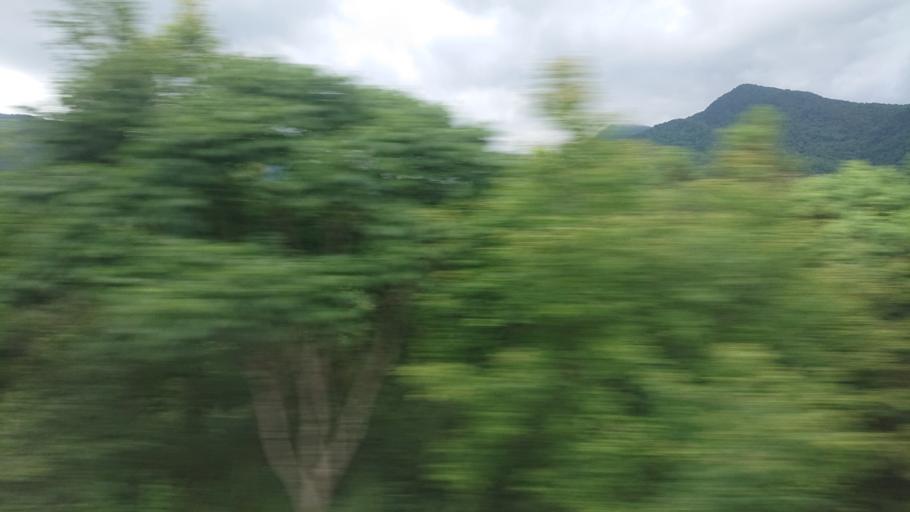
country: TW
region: Taiwan
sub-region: Hualien
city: Hualian
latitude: 23.6098
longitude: 121.3902
